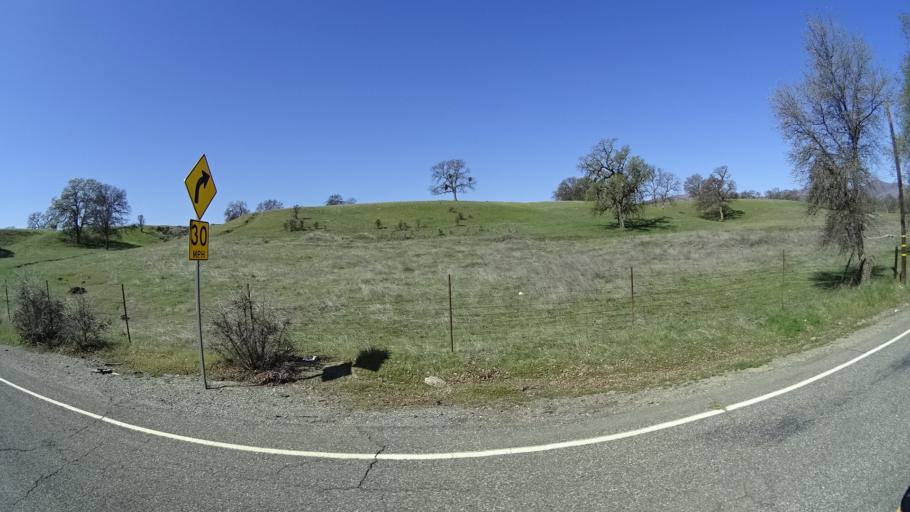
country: US
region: California
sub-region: Glenn County
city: Orland
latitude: 39.6697
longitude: -122.5254
